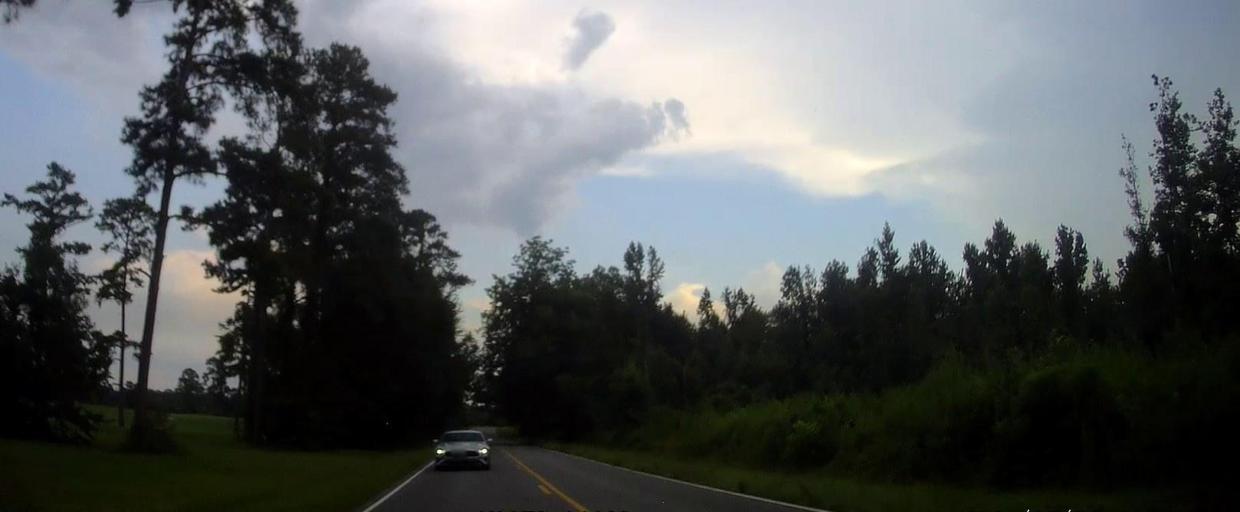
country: US
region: Georgia
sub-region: Laurens County
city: East Dublin
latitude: 32.5980
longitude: -82.8970
